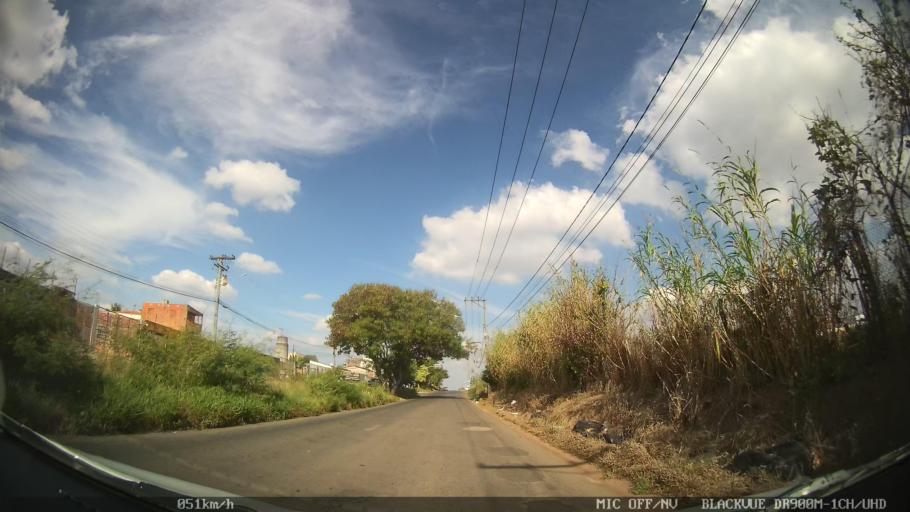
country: BR
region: Sao Paulo
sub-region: Hortolandia
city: Hortolandia
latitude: -22.9085
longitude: -47.2464
